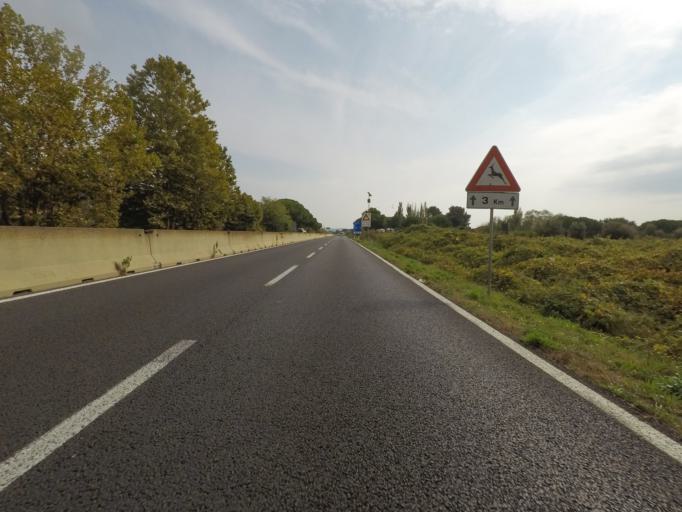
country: IT
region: Tuscany
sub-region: Provincia di Grosseto
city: Orbetello Scalo
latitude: 42.4704
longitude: 11.2368
